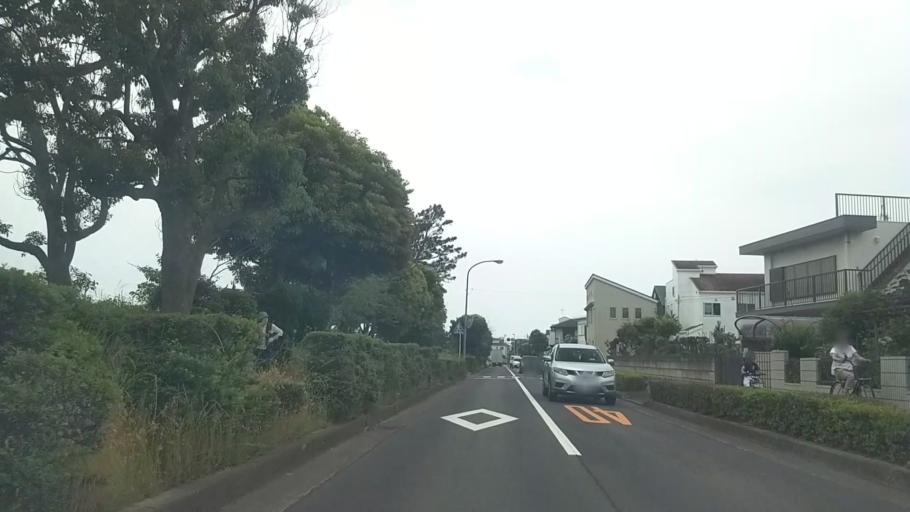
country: JP
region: Kanagawa
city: Fujisawa
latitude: 35.3242
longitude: 139.4622
